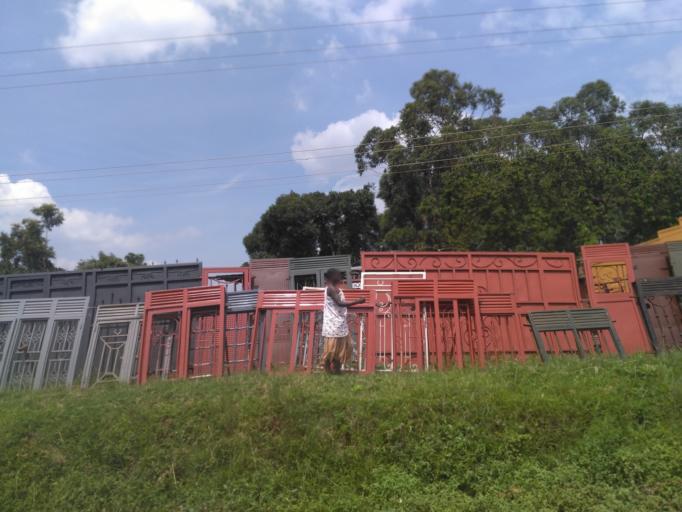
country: UG
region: Central Region
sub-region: Wakiso District
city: Bweyogerere
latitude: 0.4581
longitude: 32.6172
